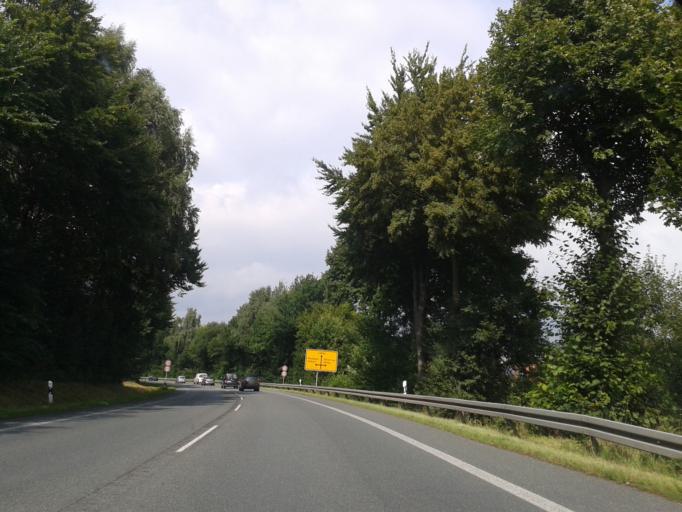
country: DE
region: North Rhine-Westphalia
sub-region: Regierungsbezirk Detmold
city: Dorentrup
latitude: 51.9857
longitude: 9.0031
